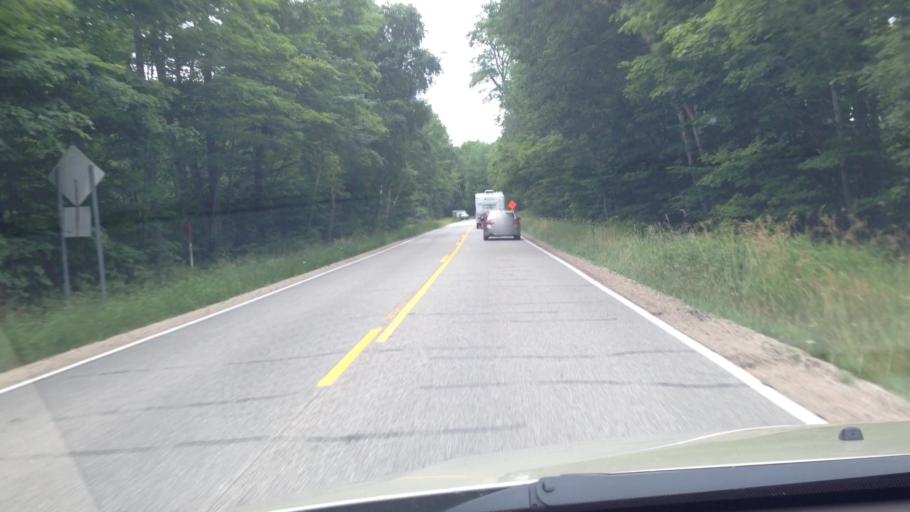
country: US
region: Michigan
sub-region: Mackinac County
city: Saint Ignace
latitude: 46.0469
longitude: -85.1089
